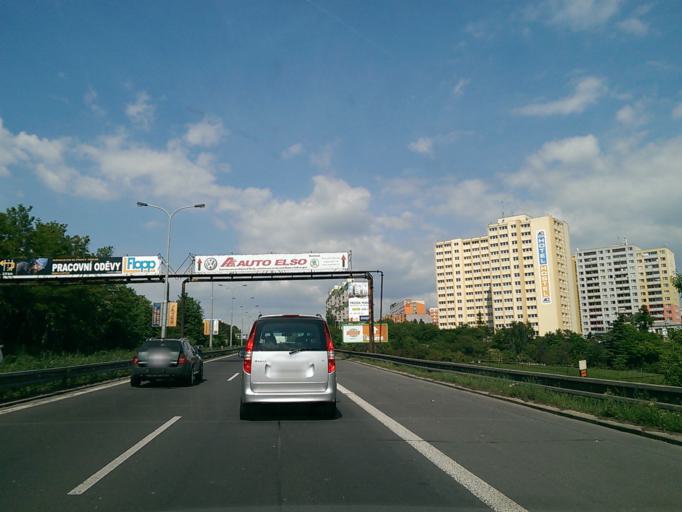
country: CZ
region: Praha
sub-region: Praha 9
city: Strizkov
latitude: 50.1237
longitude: 14.4791
